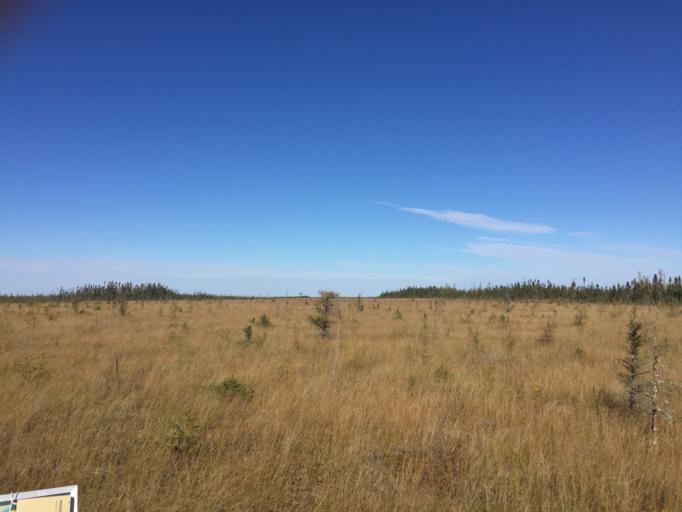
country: US
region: Minnesota
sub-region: Lake of the Woods County
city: Baudette
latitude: 48.3004
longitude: -94.5678
